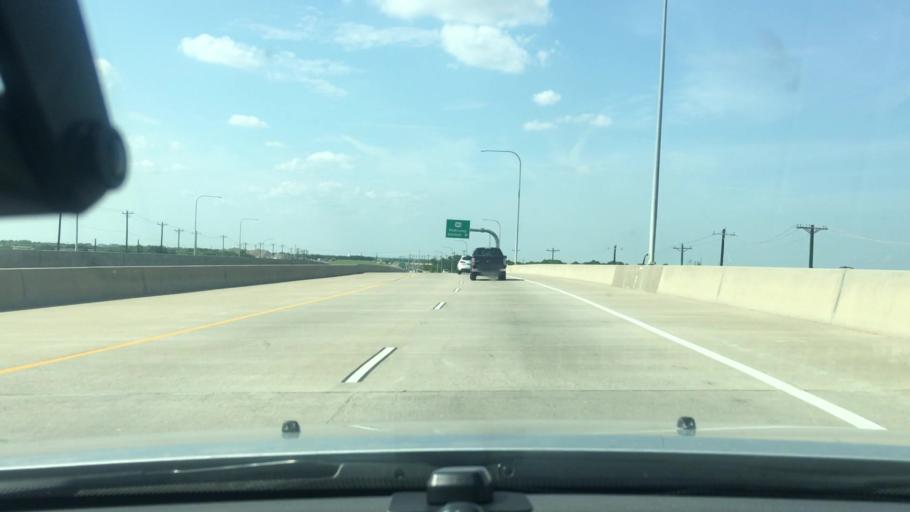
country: US
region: Texas
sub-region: Collin County
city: Prosper
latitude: 33.2085
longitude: -96.8200
